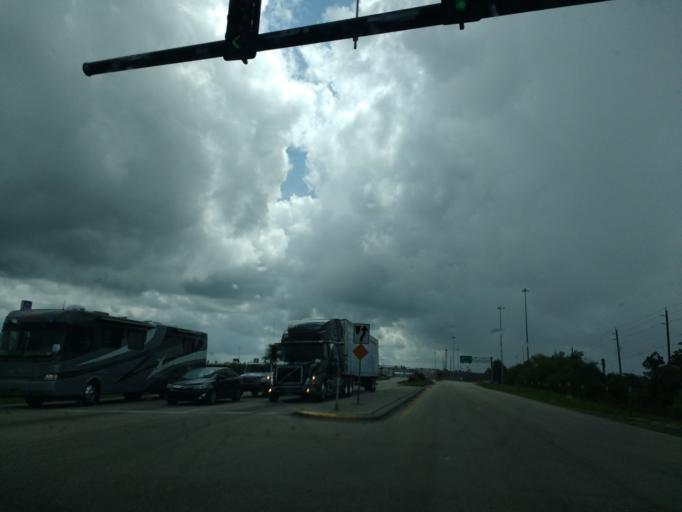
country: US
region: Florida
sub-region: Charlotte County
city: Charlotte Park
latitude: 26.8948
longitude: -82.0077
